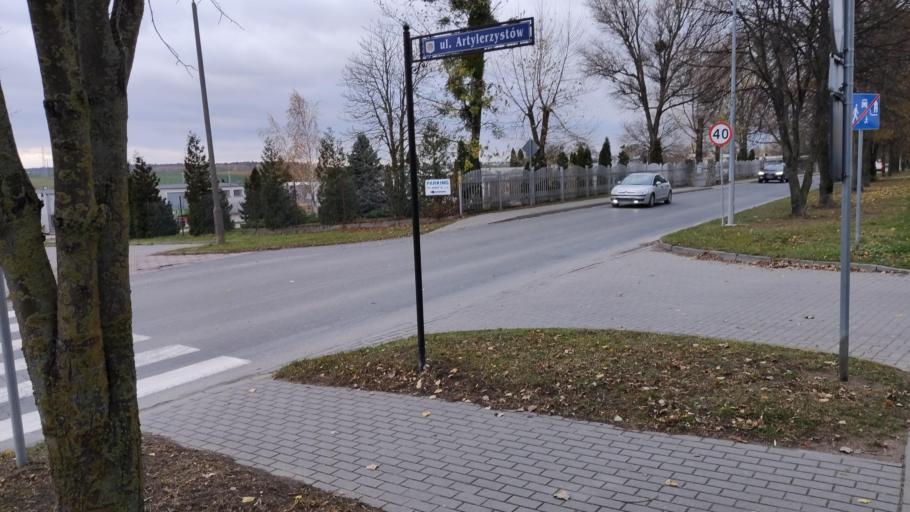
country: PL
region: Kujawsko-Pomorskie
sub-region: Powiat zninski
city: Barcin
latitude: 52.8525
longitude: 17.9504
